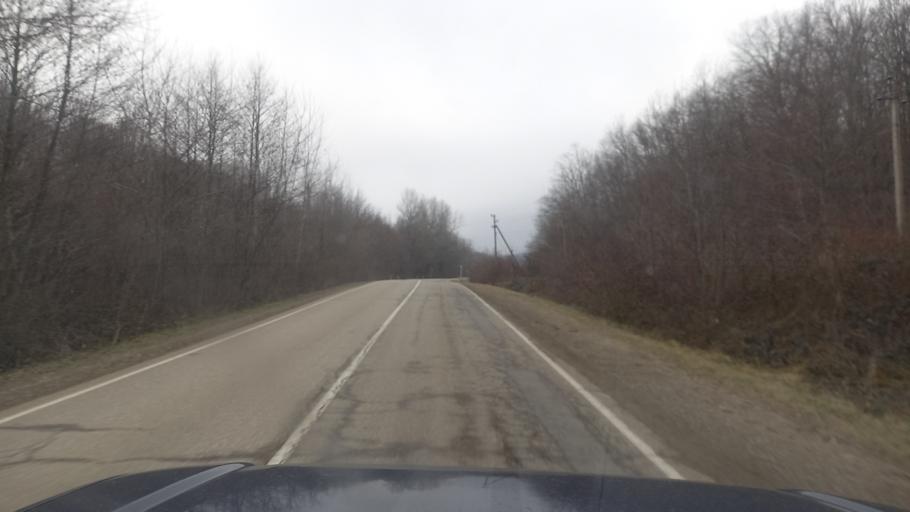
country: RU
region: Krasnodarskiy
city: Neftegorsk
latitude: 44.2832
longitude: 39.8002
